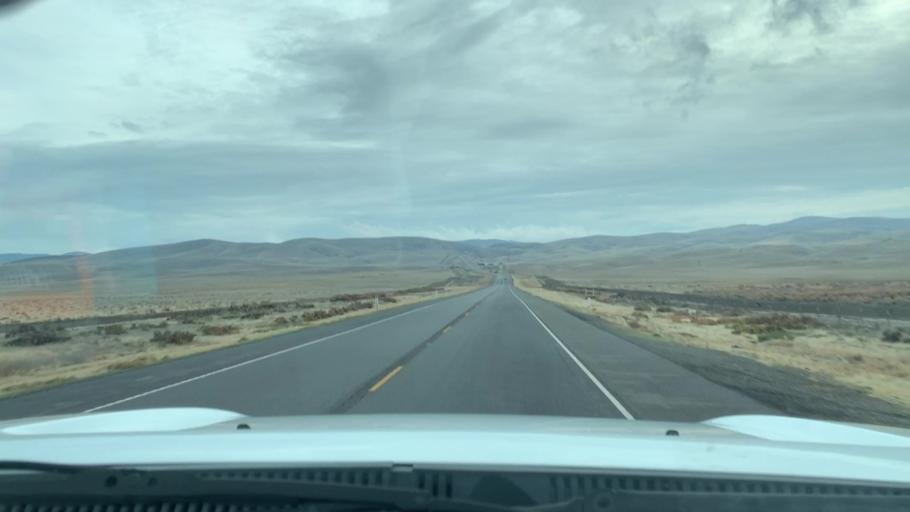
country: US
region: California
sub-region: San Luis Obispo County
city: Shandon
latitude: 35.7355
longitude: -120.2804
